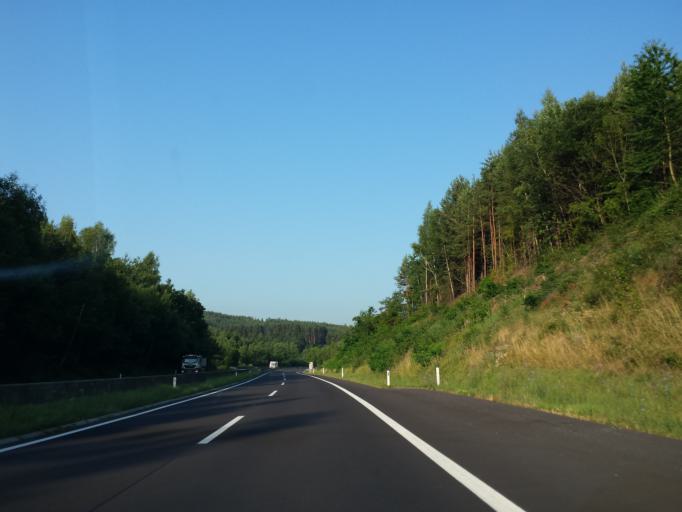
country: AT
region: Lower Austria
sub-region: Politischer Bezirk Neunkirchen
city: Wimpassing im Schwarzatale
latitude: 47.6820
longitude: 16.0326
